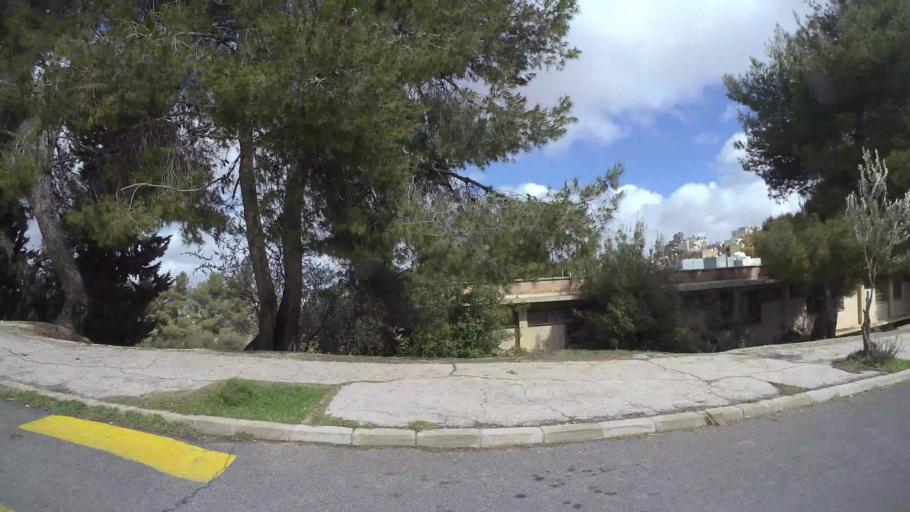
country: JO
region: Amman
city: Al Jubayhah
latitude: 32.0532
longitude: 35.8741
